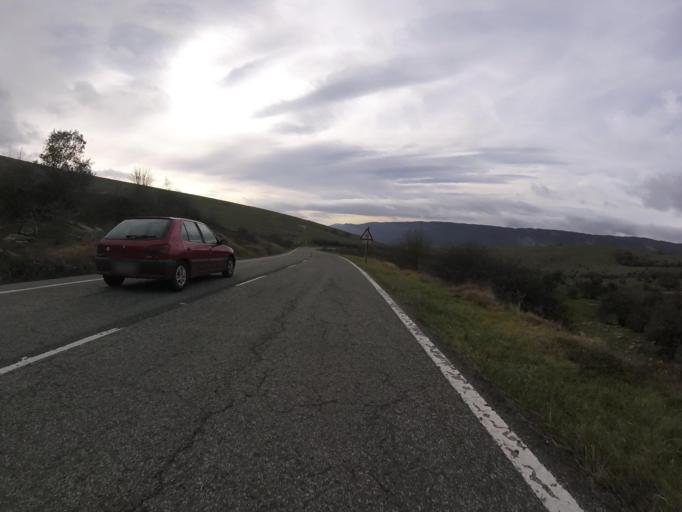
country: ES
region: Navarre
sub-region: Provincia de Navarra
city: Arbizu
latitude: 42.8545
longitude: -2.0134
